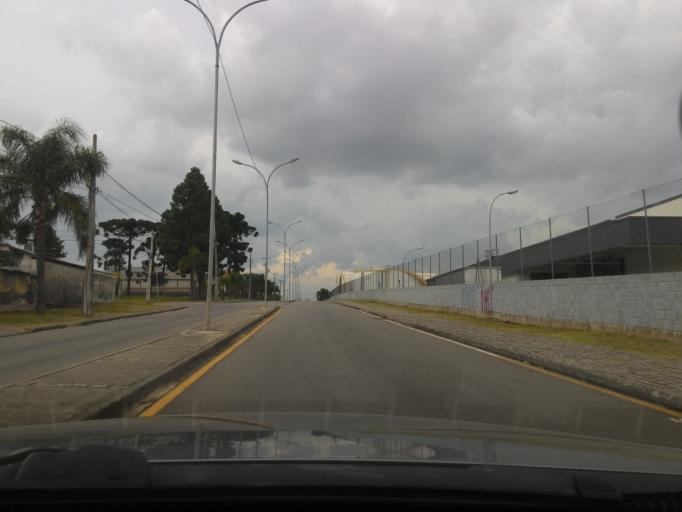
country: BR
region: Parana
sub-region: Pinhais
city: Pinhais
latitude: -25.4423
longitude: -49.1915
